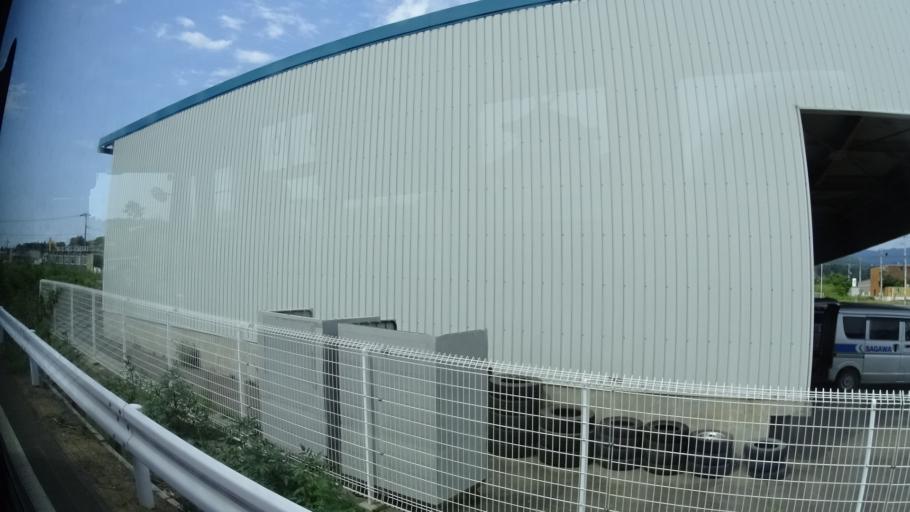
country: JP
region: Iwate
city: Ofunato
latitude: 38.8549
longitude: 141.5813
